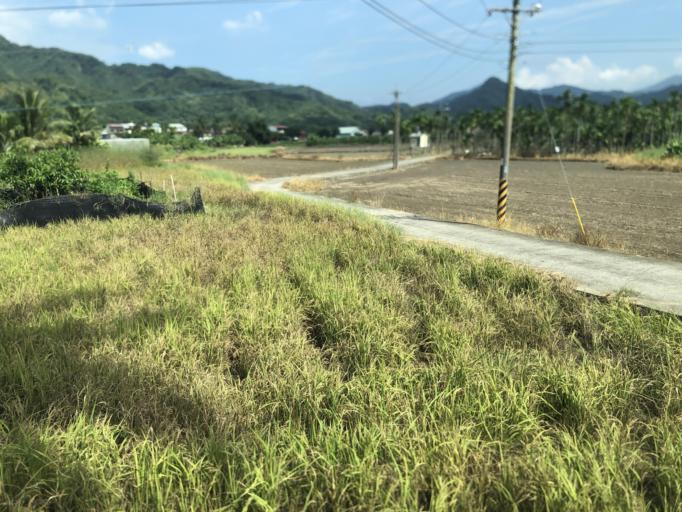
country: TW
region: Taiwan
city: Yujing
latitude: 22.9140
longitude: 120.5678
